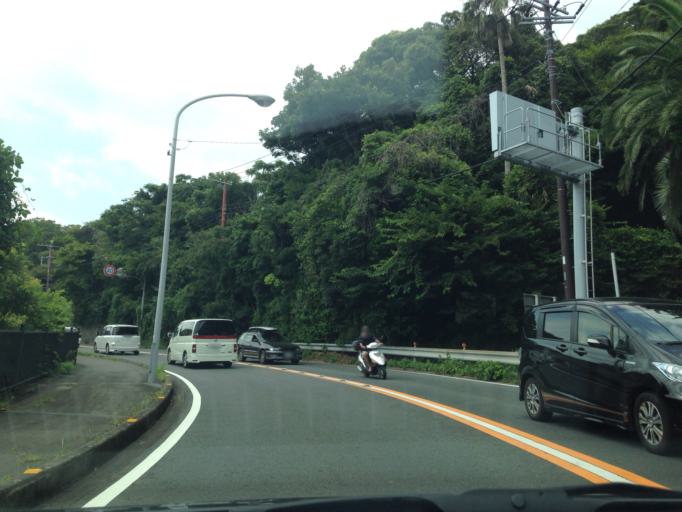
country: JP
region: Shizuoka
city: Shimoda
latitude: 34.7345
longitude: 138.9973
